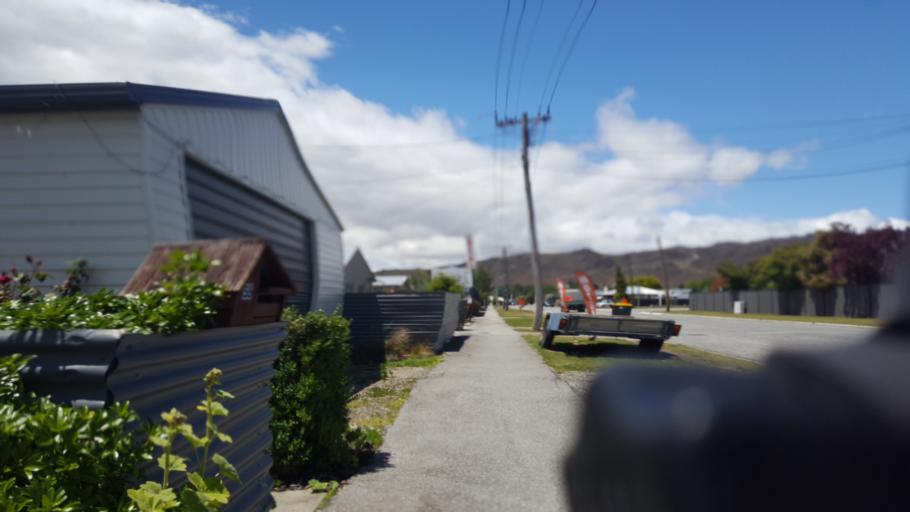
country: NZ
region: Otago
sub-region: Queenstown-Lakes District
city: Wanaka
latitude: -45.2481
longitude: 169.3880
